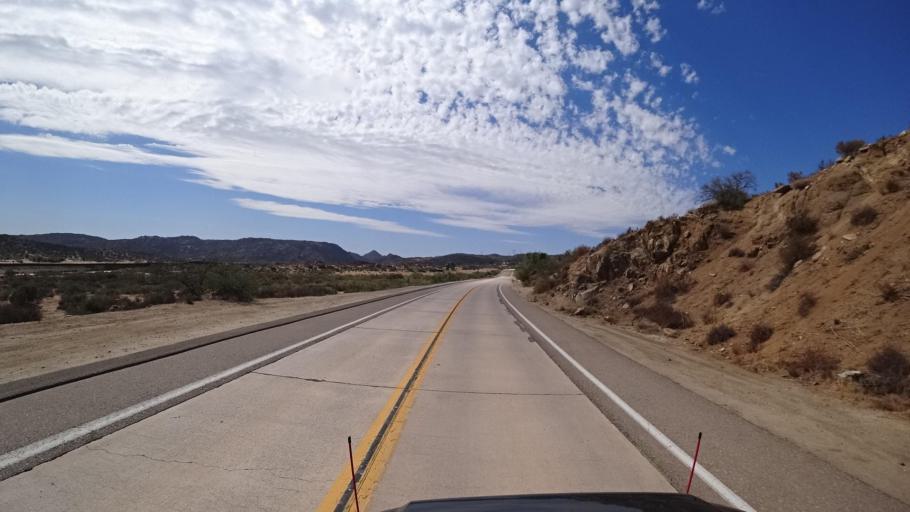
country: MX
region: Baja California
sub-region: Tecate
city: Cereso del Hongo
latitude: 32.6123
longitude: -116.2038
